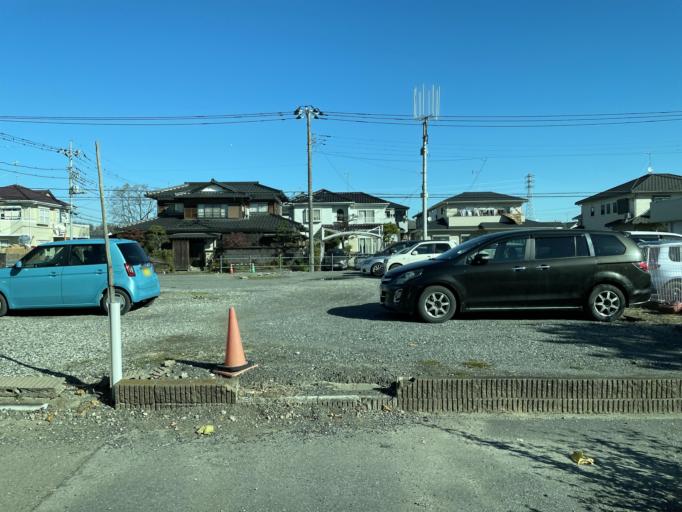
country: JP
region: Saitama
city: Kukichuo
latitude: 36.0691
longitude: 139.6984
